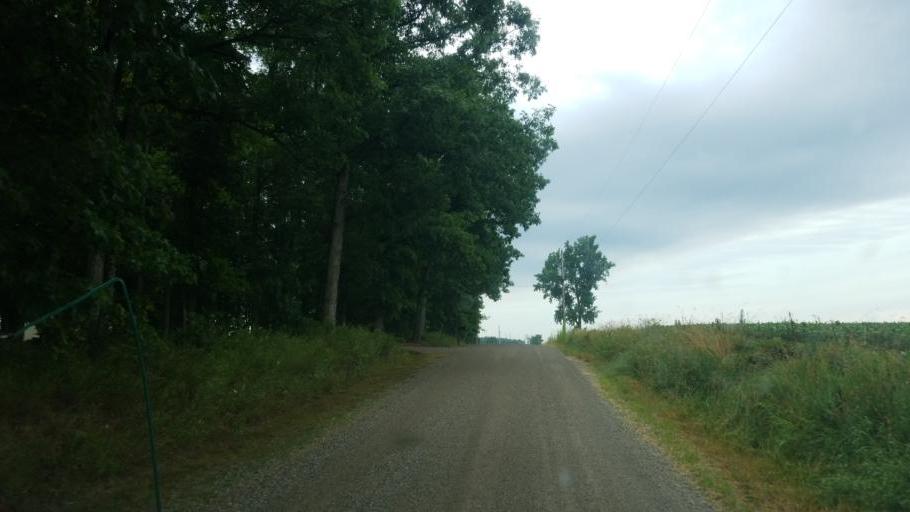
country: US
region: Indiana
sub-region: Steuben County
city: Hamilton
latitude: 41.5020
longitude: -84.9112
